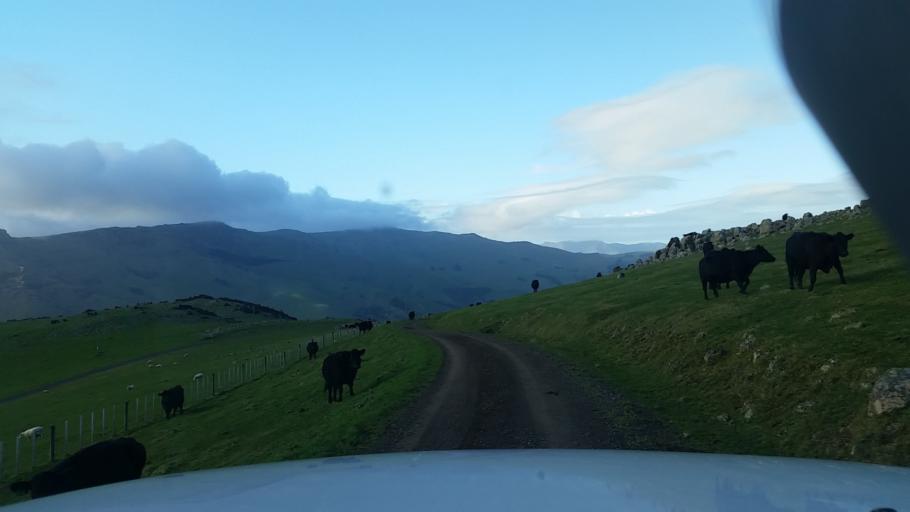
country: NZ
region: Canterbury
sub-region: Christchurch City
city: Christchurch
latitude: -43.6575
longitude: 172.8777
